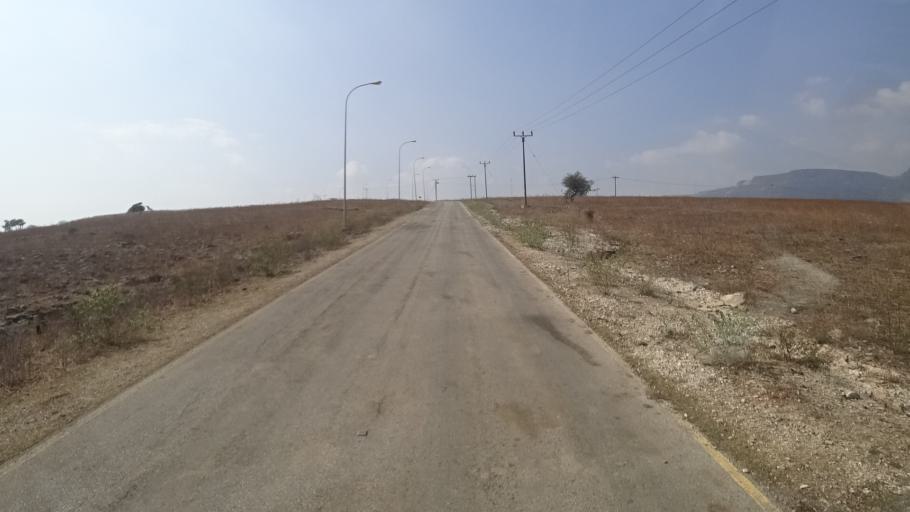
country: YE
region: Al Mahrah
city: Hawf
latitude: 16.7306
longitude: 53.2665
